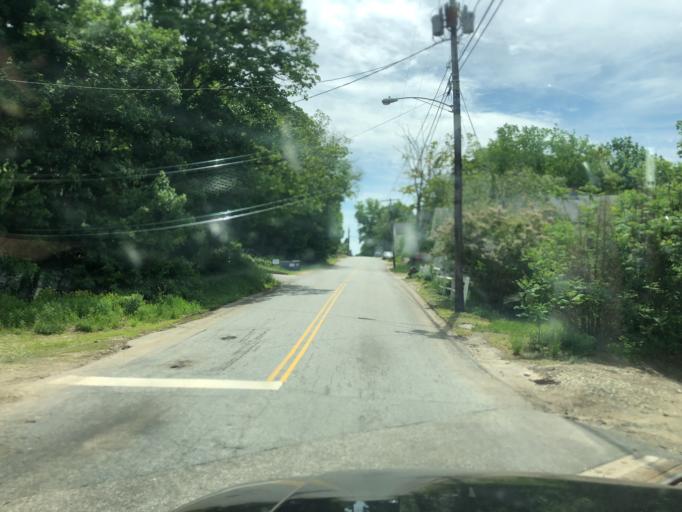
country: US
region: Connecticut
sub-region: Windham County
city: North Grosvenor Dale
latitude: 41.9877
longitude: -71.8952
